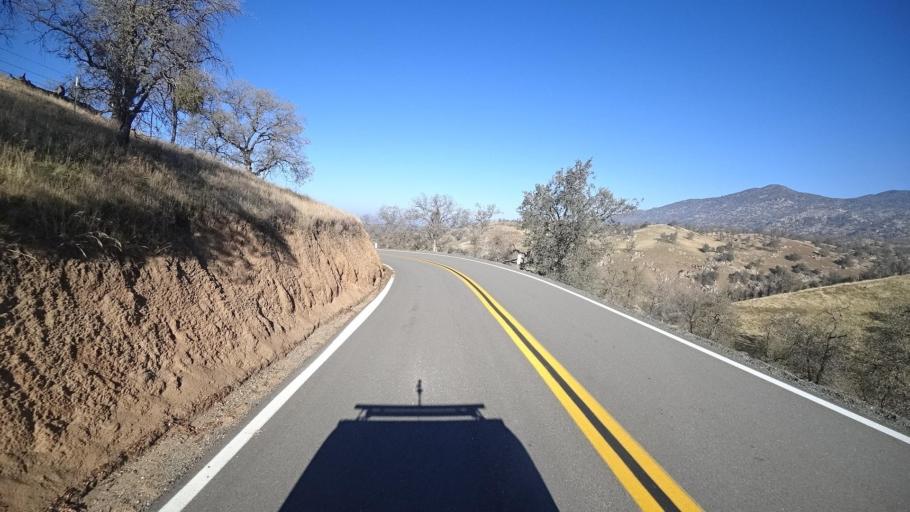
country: US
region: California
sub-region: Kern County
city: Alta Sierra
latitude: 35.7218
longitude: -118.7999
